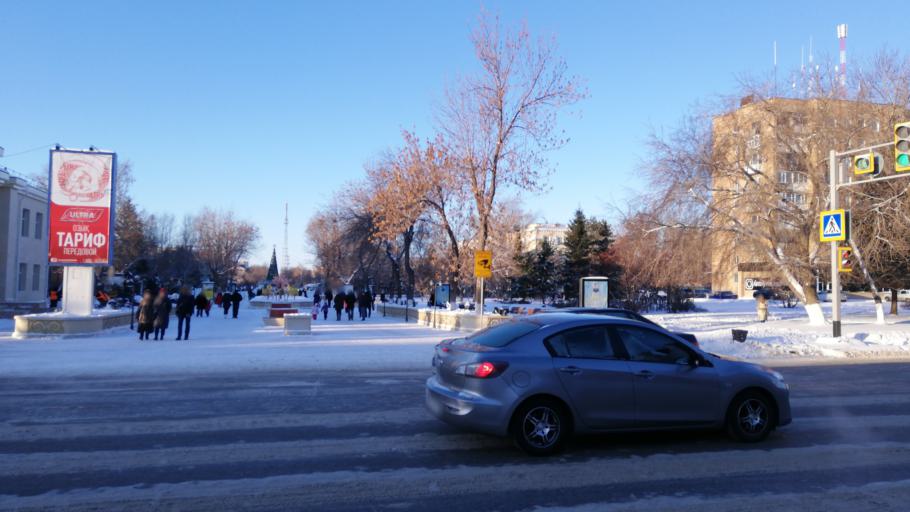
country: KZ
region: Soltustik Qazaqstan
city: Petropavlovsk
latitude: 54.8654
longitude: 69.1358
